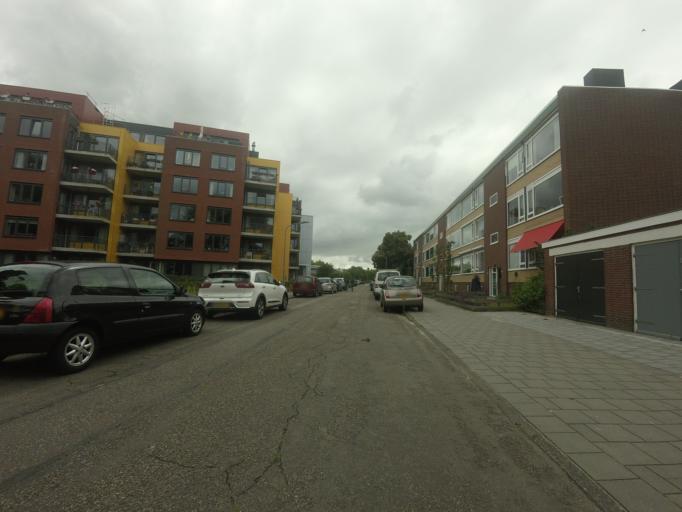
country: NL
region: North Holland
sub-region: Gemeente Bloemendaal
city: Bloemendaal
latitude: 52.4104
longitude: 4.6407
